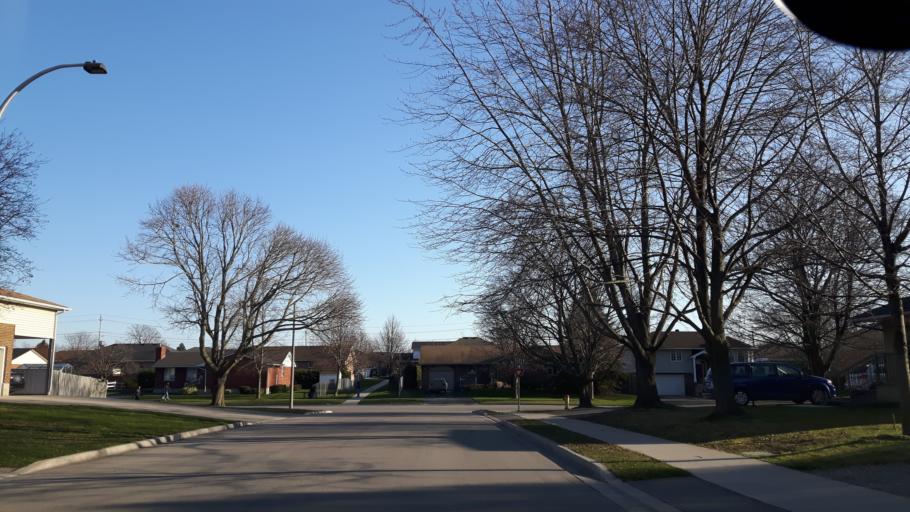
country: CA
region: Ontario
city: Goderich
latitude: 43.7306
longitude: -81.7141
